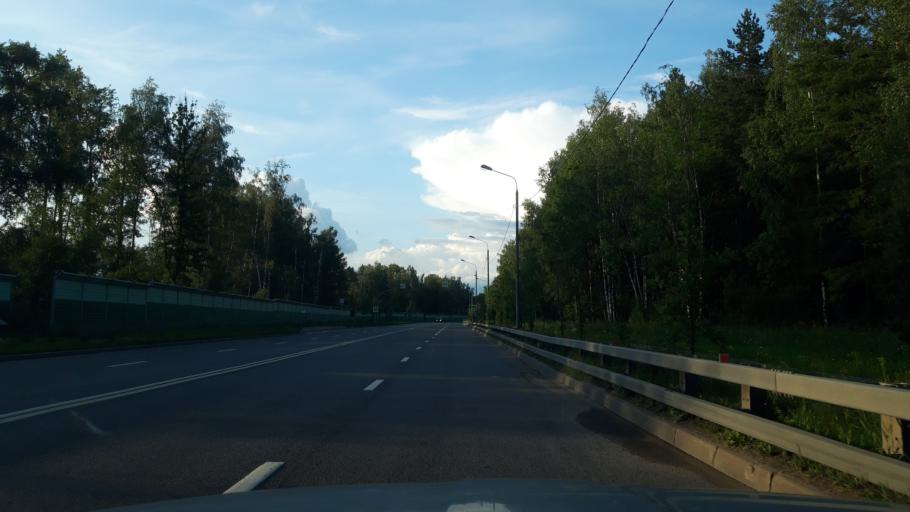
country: RU
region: Moskovskaya
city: Alabushevo
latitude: 56.0003
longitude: 37.1628
